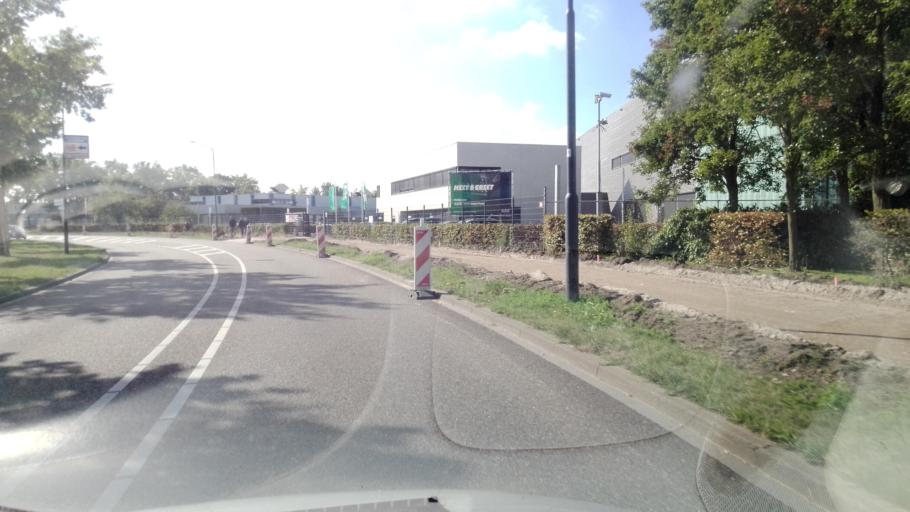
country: NL
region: North Brabant
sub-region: Gemeente Helmond
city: Helmond
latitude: 51.4590
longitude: 5.6914
